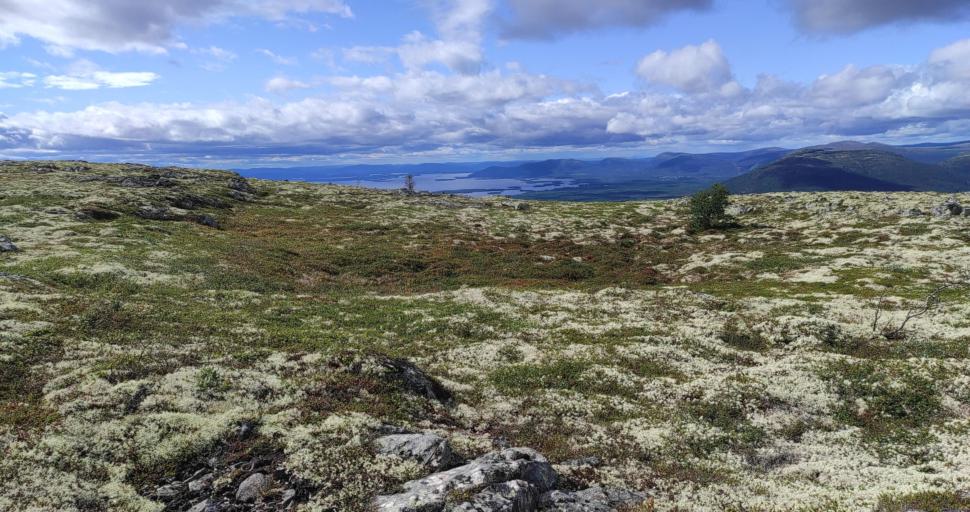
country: RU
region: Murmansk
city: Afrikanda
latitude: 67.0452
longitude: 32.9520
